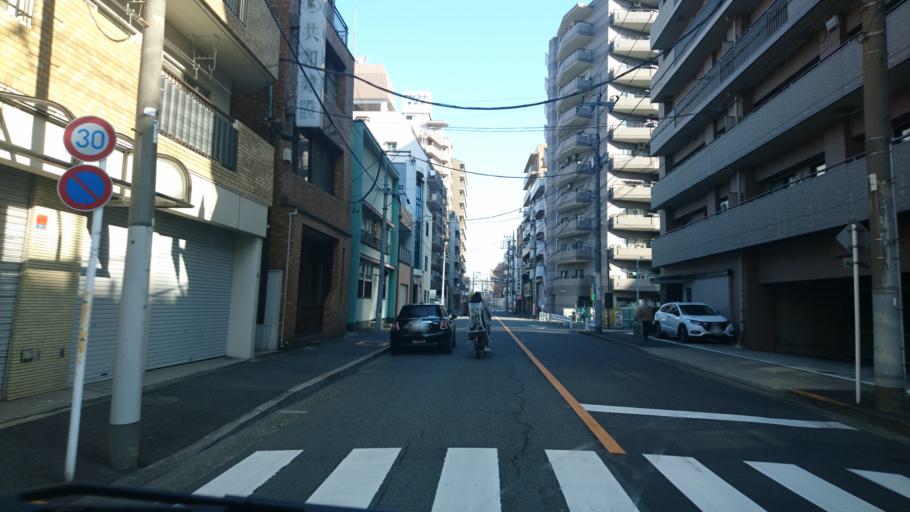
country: JP
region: Kanagawa
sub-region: Kawasaki-shi
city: Kawasaki
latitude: 35.5622
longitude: 139.7088
